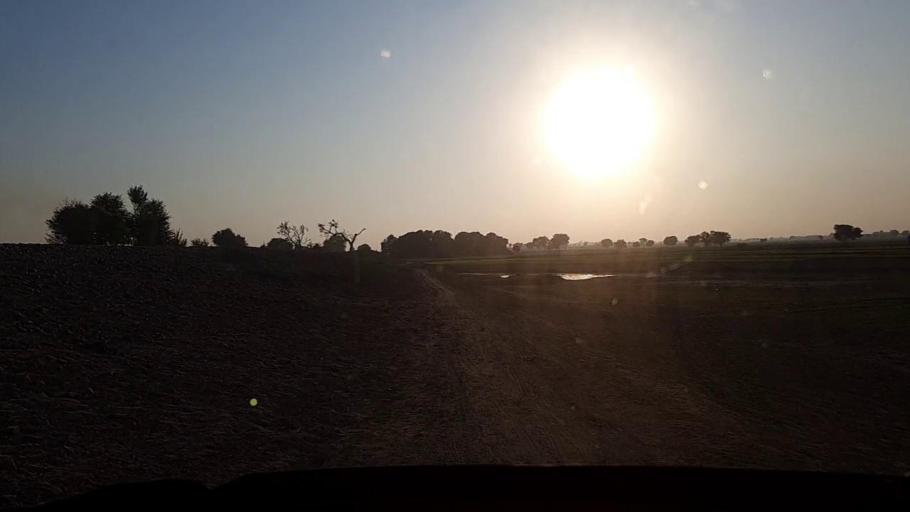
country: PK
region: Sindh
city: Sobhadero
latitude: 27.3679
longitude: 68.3768
